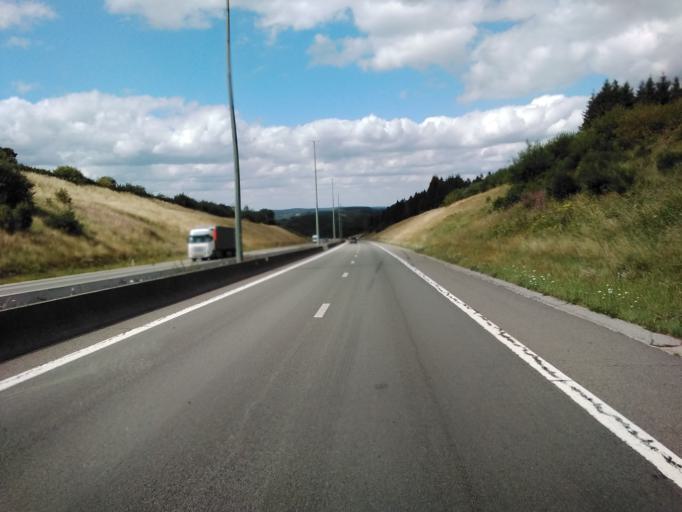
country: BE
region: Wallonia
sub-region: Province du Luxembourg
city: Manhay
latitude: 50.2812
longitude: 5.7282
